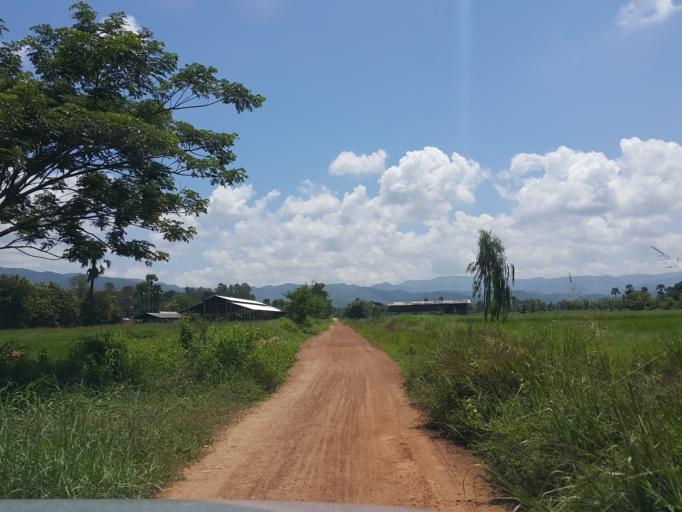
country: TH
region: Lamphun
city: Ban Thi
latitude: 18.6722
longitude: 99.1438
